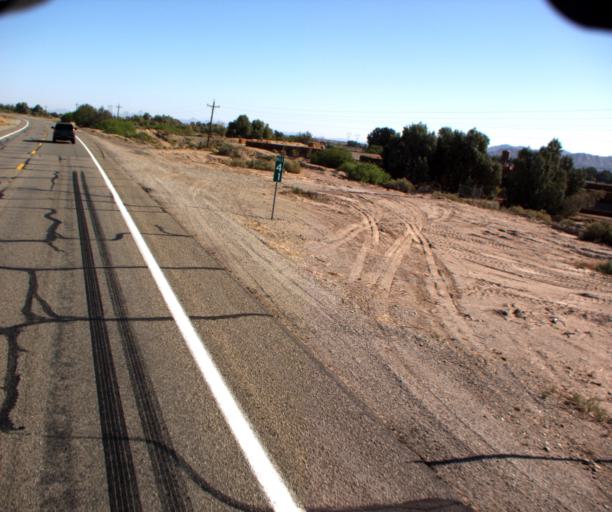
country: US
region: Arizona
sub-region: Yuma County
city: Fortuna Foothills
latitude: 32.7781
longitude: -114.3841
